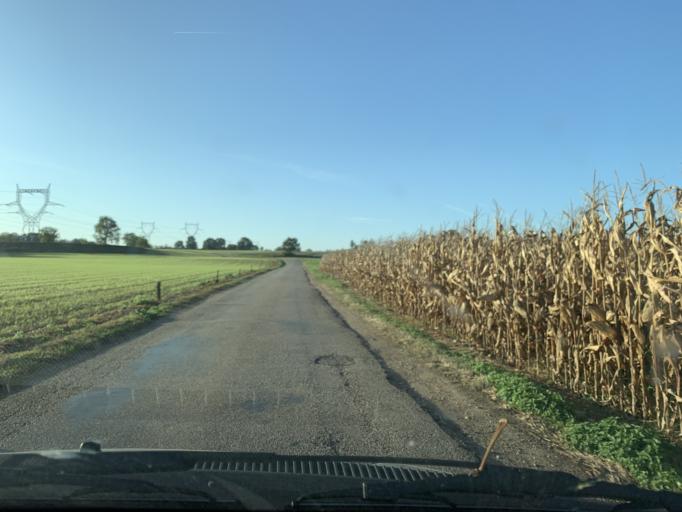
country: FR
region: Rhone-Alpes
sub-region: Departement de l'Ain
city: Saint-Maurice-de-Gourdans
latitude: 45.8394
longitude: 5.1974
